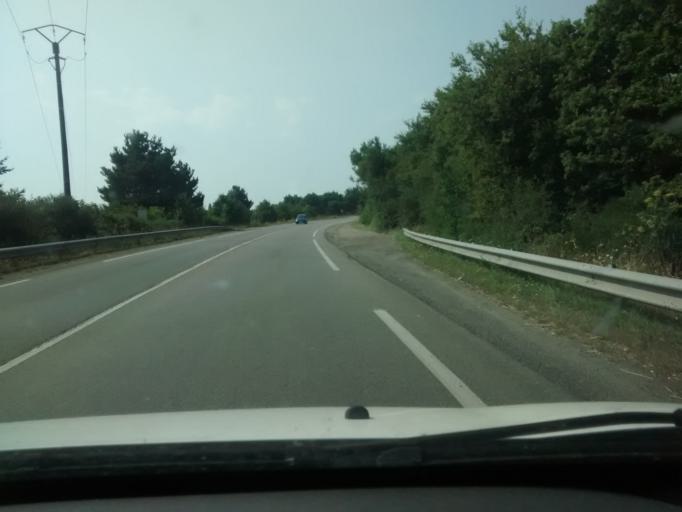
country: FR
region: Pays de la Loire
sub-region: Departement de la Loire-Atlantique
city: Saint-Andre-des-Eaux
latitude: 47.2828
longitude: -2.3015
